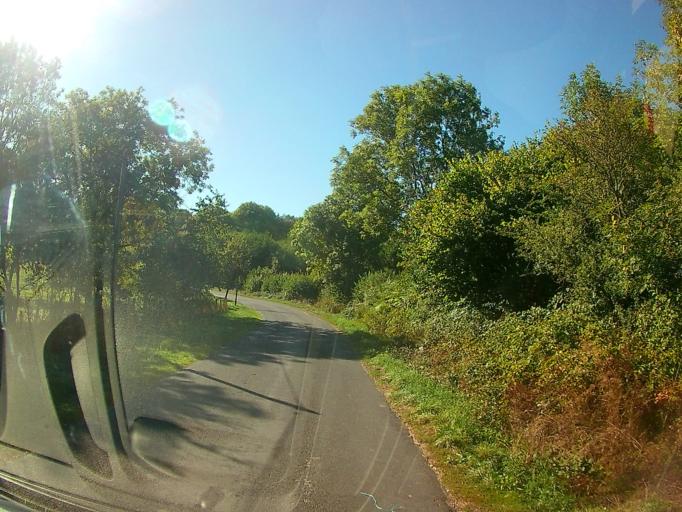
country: FR
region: Auvergne
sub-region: Departement du Puy-de-Dome
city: Chapdes-Beaufort
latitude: 45.8958
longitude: 2.8726
